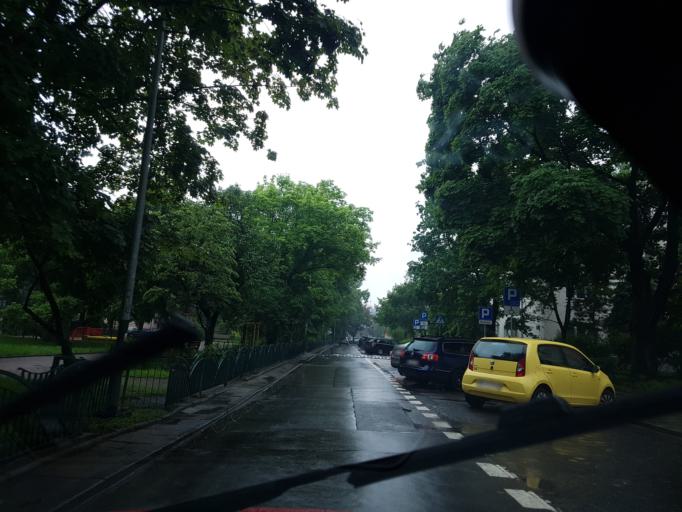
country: PL
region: Lesser Poland Voivodeship
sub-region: Krakow
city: Krakow
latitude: 50.0565
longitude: 19.9527
